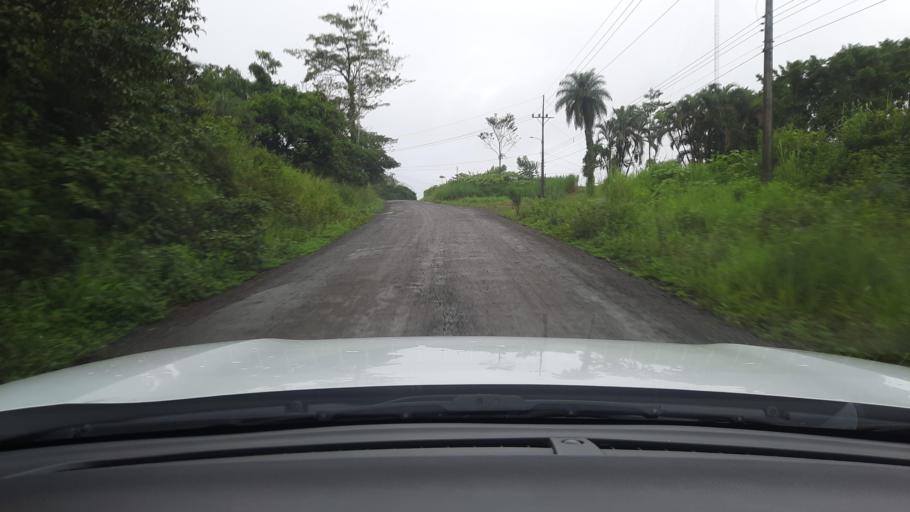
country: CR
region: Alajuela
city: San Jose
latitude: 11.0127
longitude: -85.3264
